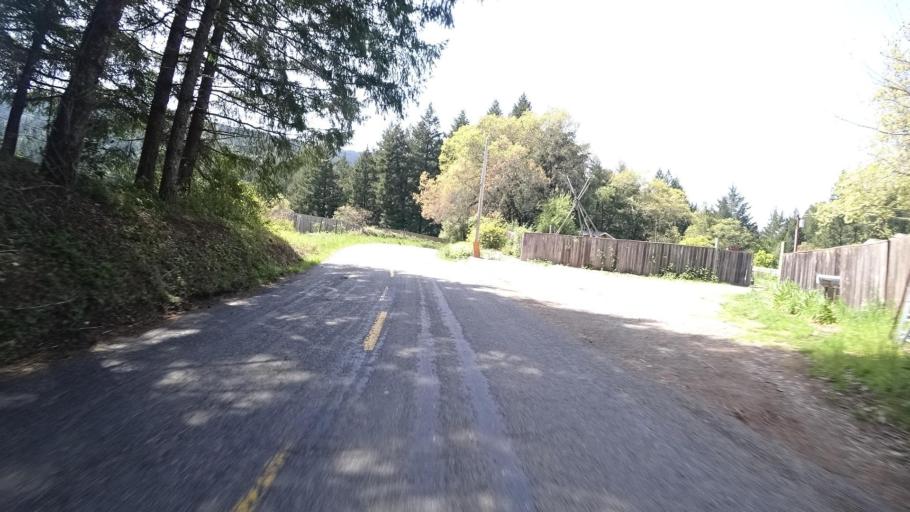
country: US
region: California
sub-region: Humboldt County
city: Redway
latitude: 40.3619
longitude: -123.7278
